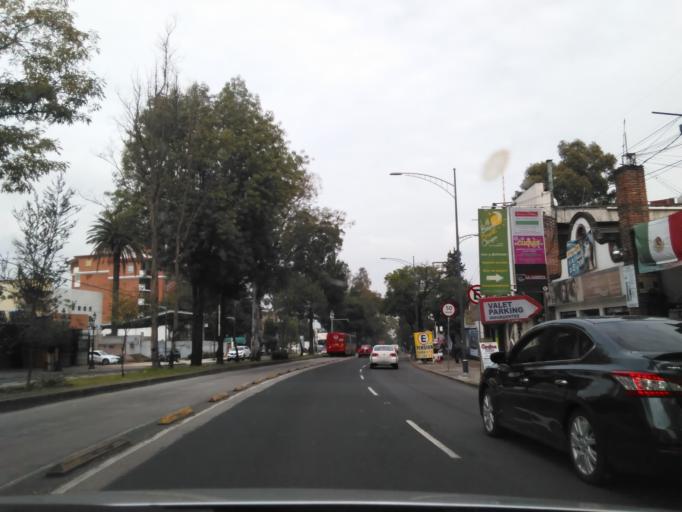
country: MX
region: Mexico City
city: Tlalpan
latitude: 19.2853
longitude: -99.1756
